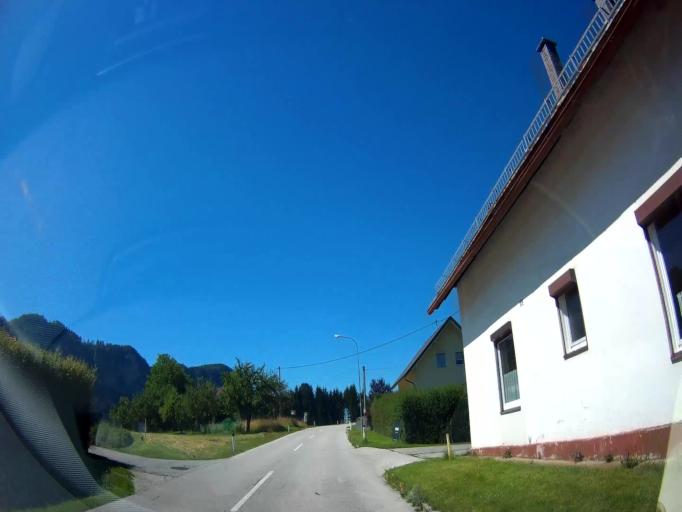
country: AT
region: Carinthia
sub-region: Politischer Bezirk Volkermarkt
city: Gallizien
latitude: 46.5723
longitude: 14.5070
